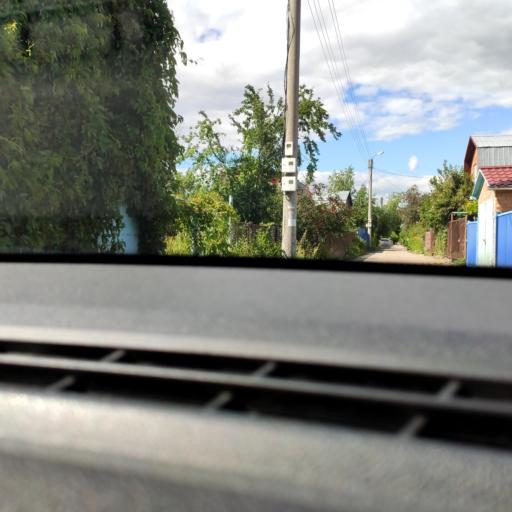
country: RU
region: Samara
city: Podstepki
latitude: 53.5829
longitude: 49.0688
